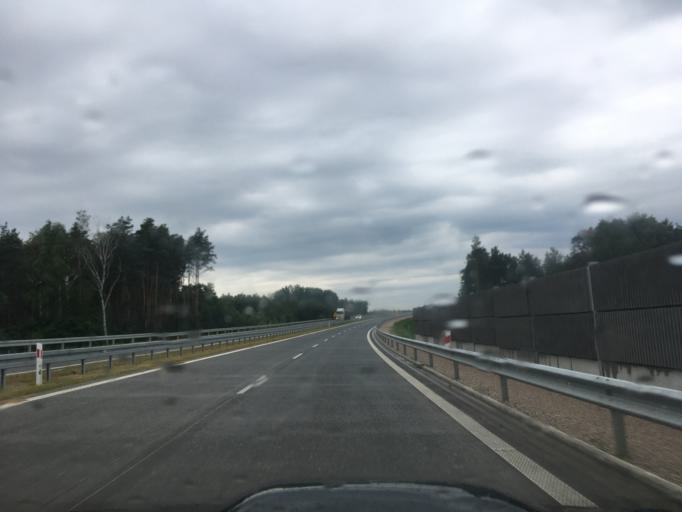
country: PL
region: Masovian Voivodeship
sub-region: Powiat piaseczynski
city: Gora Kalwaria
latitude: 51.9824
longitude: 21.1761
